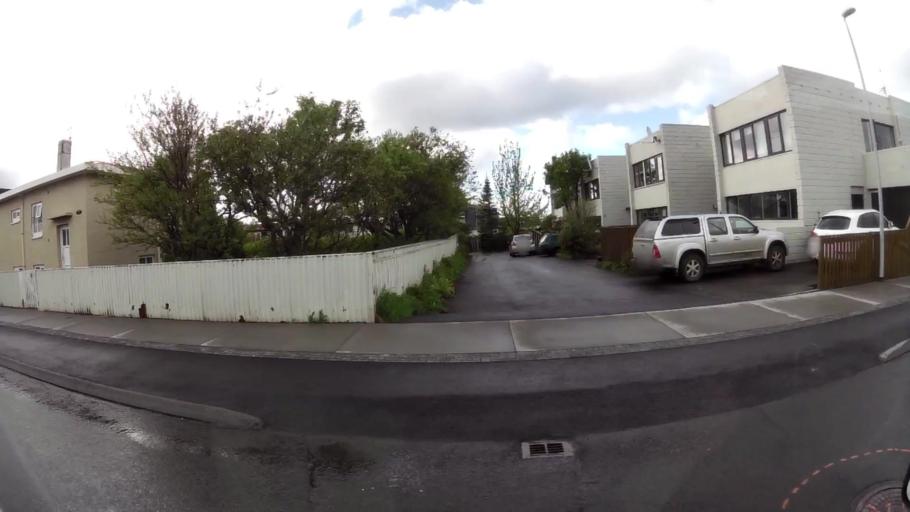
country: IS
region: Capital Region
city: Seltjarnarnes
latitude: 64.1311
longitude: -21.9557
